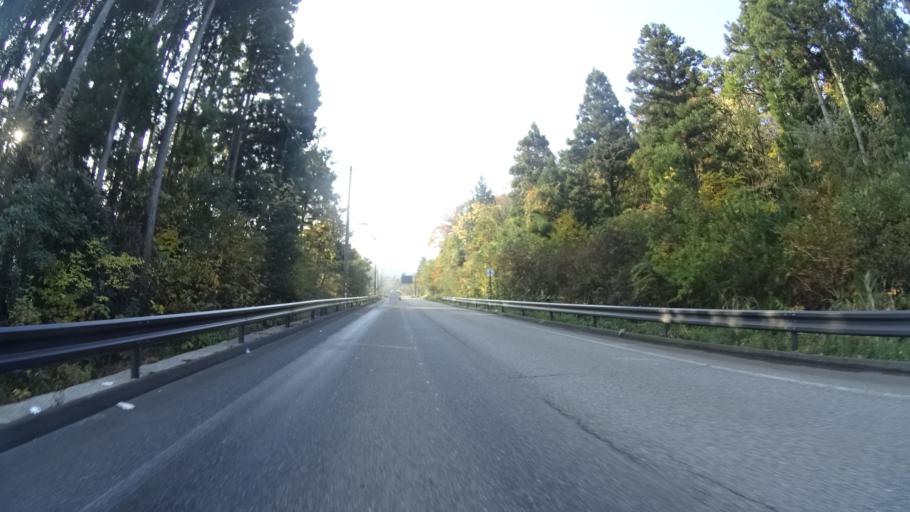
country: JP
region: Ishikawa
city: Nanao
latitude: 37.0261
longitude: 136.9854
